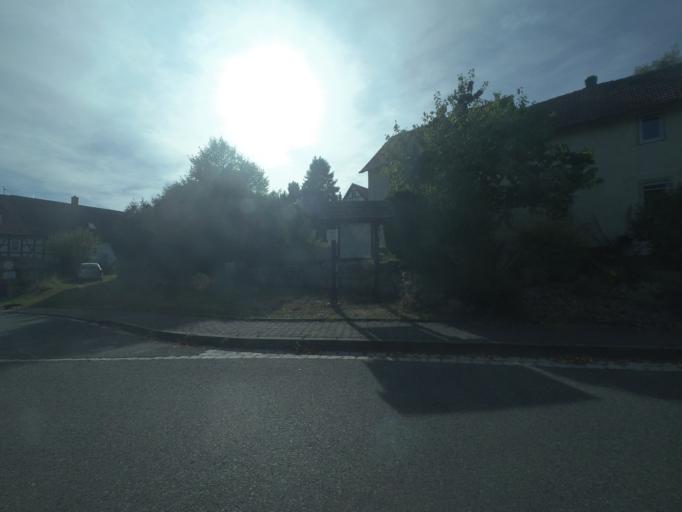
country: DE
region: Thuringia
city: Melpers
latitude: 50.5482
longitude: 10.1965
